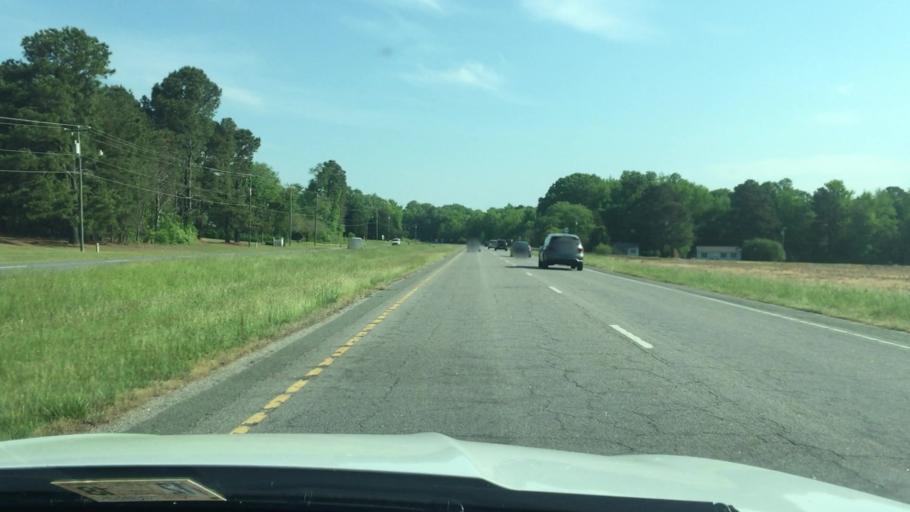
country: US
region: Virginia
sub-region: Lancaster County
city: Kilmarnock
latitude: 37.6928
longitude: -76.3749
